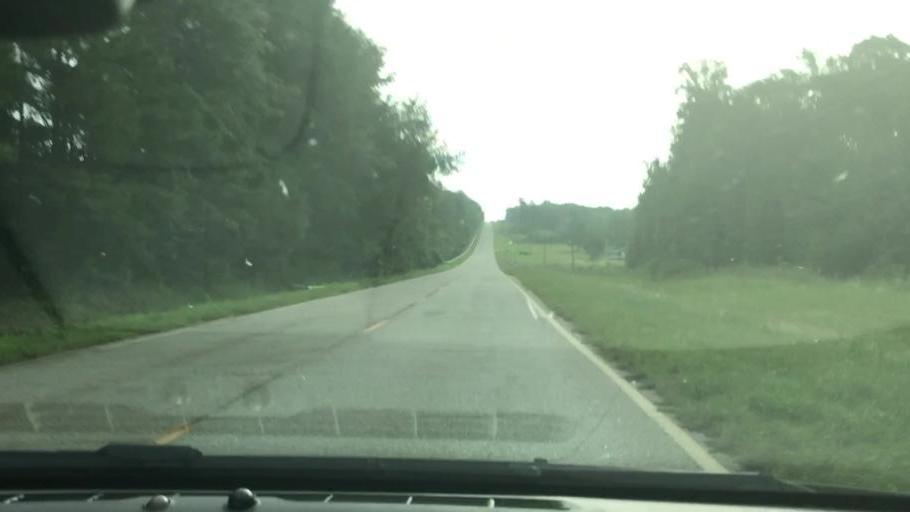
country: US
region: Georgia
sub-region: Quitman County
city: Georgetown
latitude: 31.8933
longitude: -85.0735
